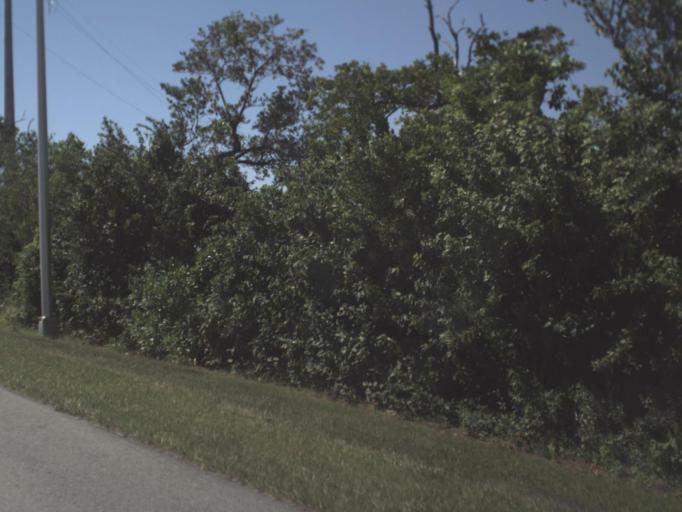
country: US
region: Florida
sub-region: Collier County
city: Marco
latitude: 25.9677
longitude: -81.7082
